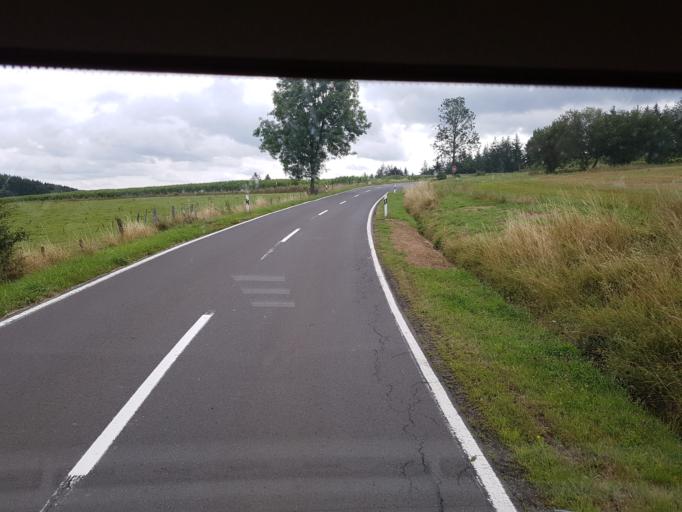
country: DE
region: Rheinland-Pfalz
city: Winterspelt
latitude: 50.2314
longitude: 6.1921
